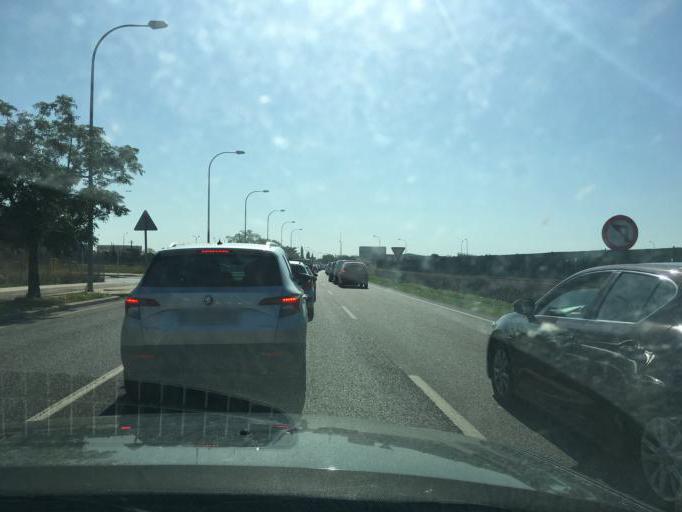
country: ES
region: Balearic Islands
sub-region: Illes Balears
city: Palma
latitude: 39.5725
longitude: 2.6856
